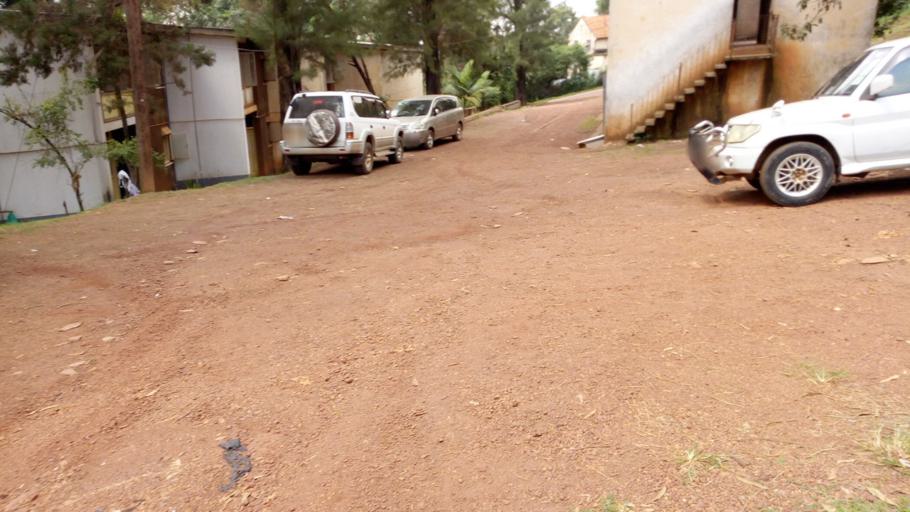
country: UG
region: Central Region
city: Kampala Central Division
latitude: 0.3386
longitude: 32.5656
